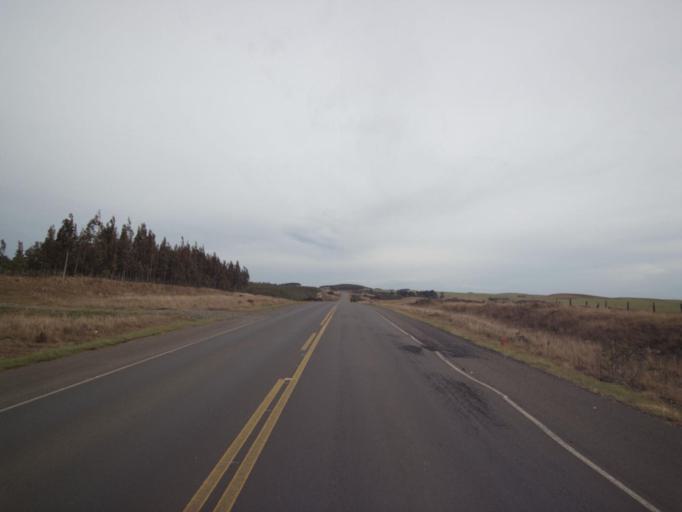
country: BR
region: Parana
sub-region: Palmas
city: Palmas
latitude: -26.7366
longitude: -51.6493
